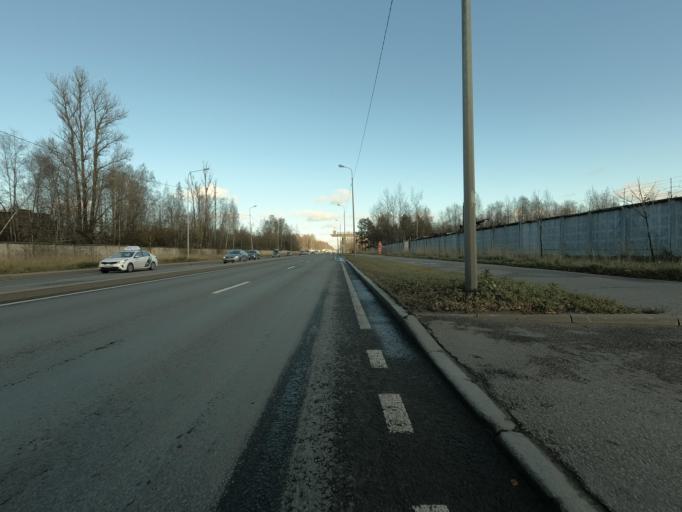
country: RU
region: St.-Petersburg
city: Krasnogvargeisky
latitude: 59.9904
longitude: 30.5300
